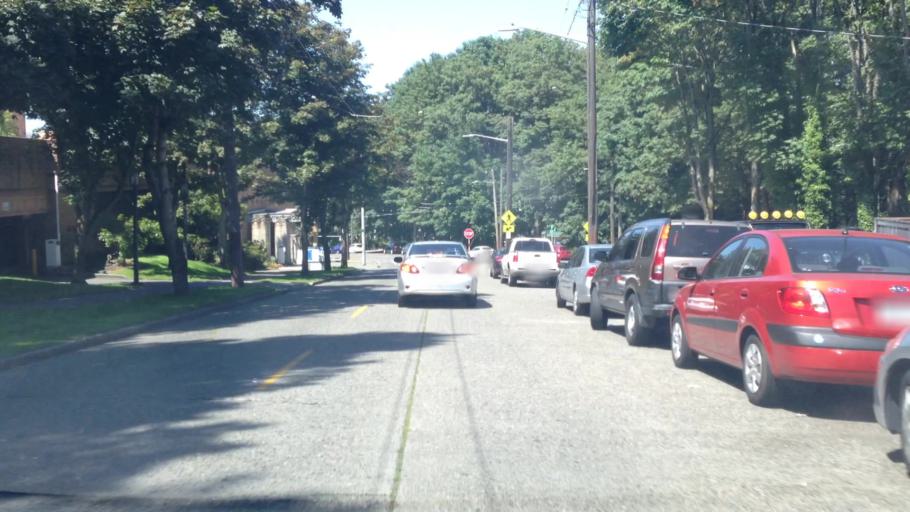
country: US
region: Washington
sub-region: King County
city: Seattle
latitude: 47.5919
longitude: -122.3149
